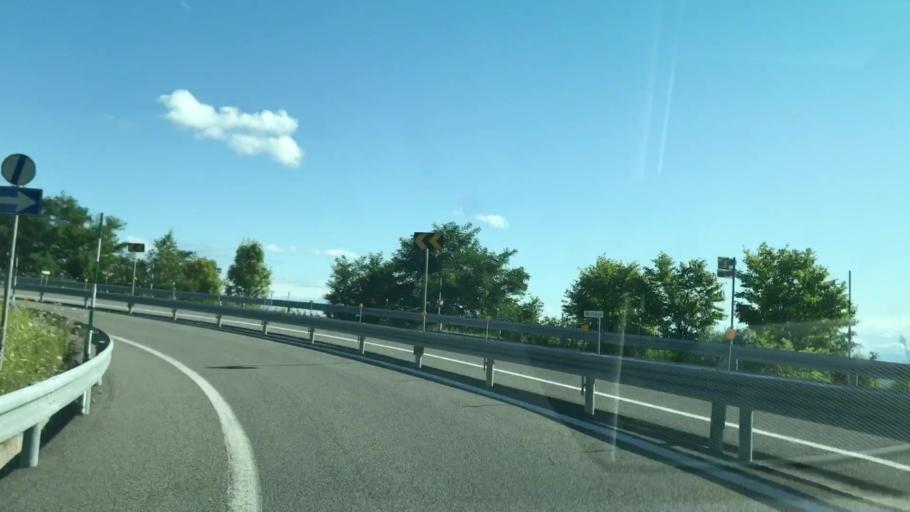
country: JP
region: Hokkaido
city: Date
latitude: 42.5573
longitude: 140.7712
